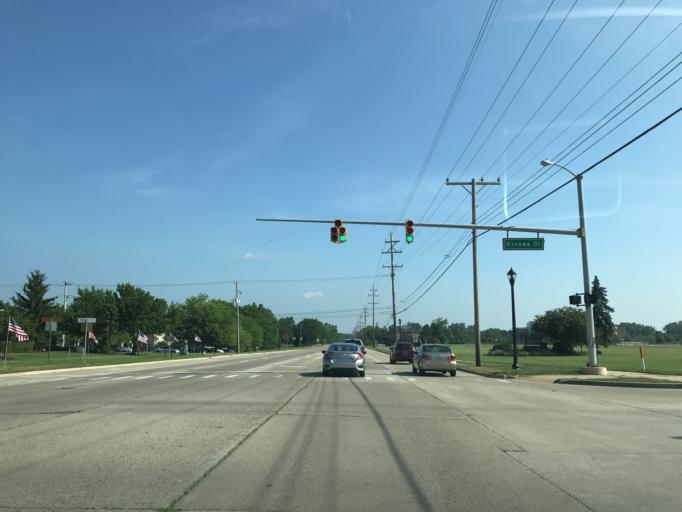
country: US
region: Michigan
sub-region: Ingham County
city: Okemos
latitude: 42.6967
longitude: -84.4324
